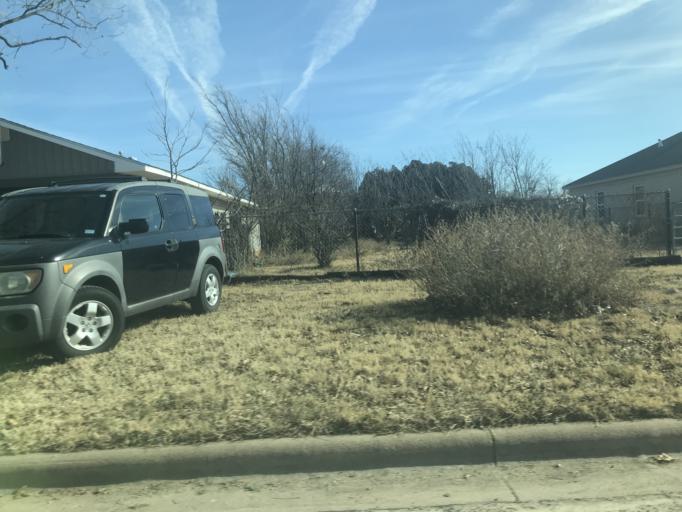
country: US
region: Texas
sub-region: Taylor County
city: Abilene
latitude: 32.4882
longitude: -99.7361
